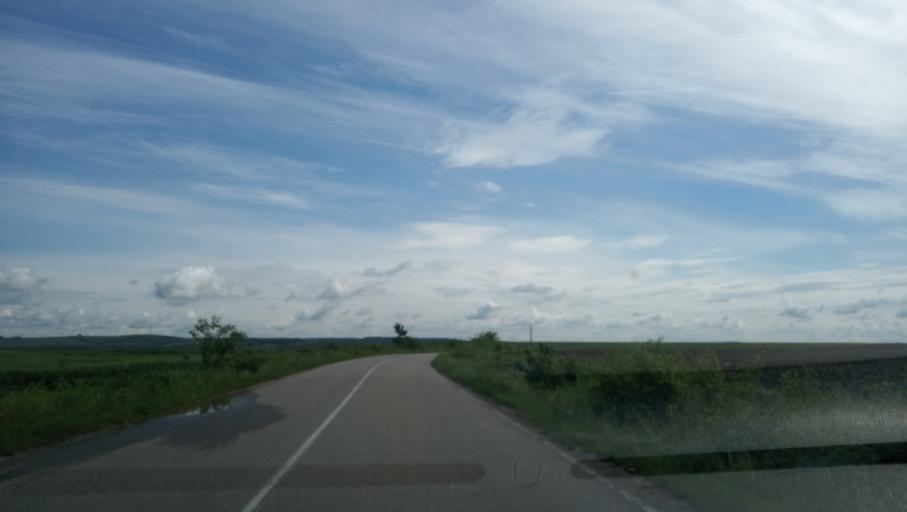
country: RO
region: Timis
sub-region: Comuna Topolovatu Mare
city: Topolovatu Mare
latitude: 45.7852
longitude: 21.6448
